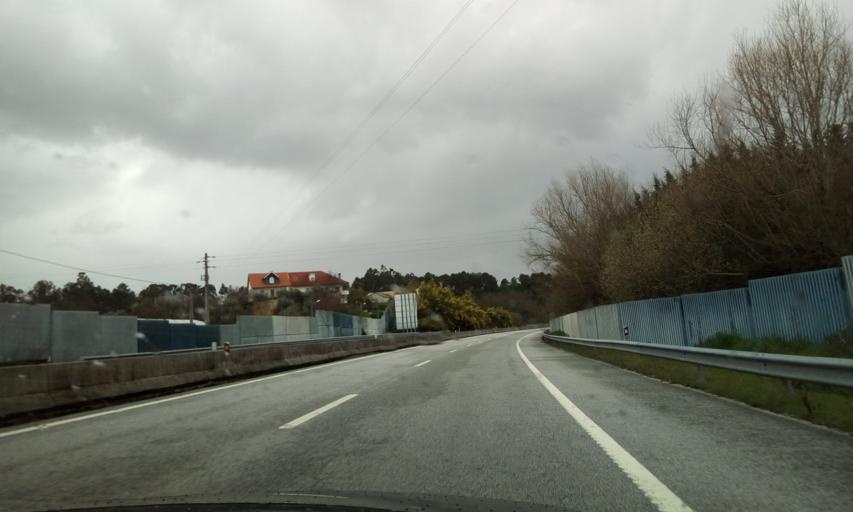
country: PT
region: Viseu
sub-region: Viseu
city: Rio de Loba
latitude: 40.6456
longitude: -7.8701
